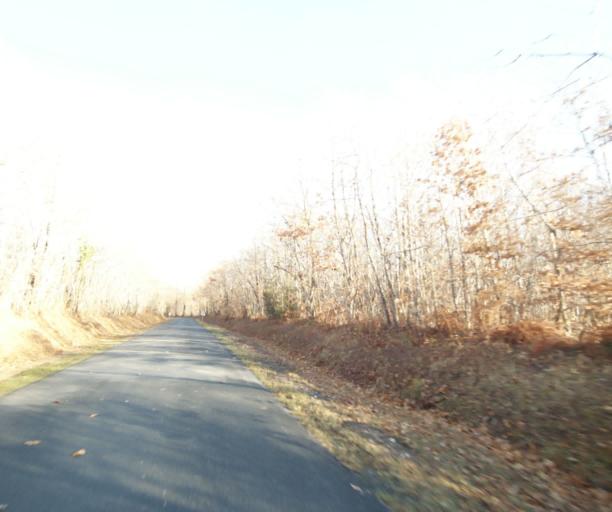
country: FR
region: Poitou-Charentes
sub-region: Departement de la Charente-Maritime
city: Cherac
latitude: 45.7191
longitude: -0.4630
